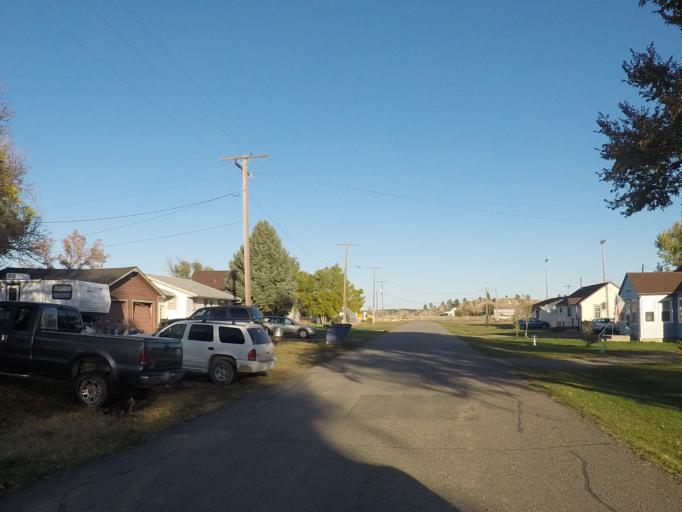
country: US
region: Montana
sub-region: Golden Valley County
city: Ryegate
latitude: 46.2936
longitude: -108.9362
